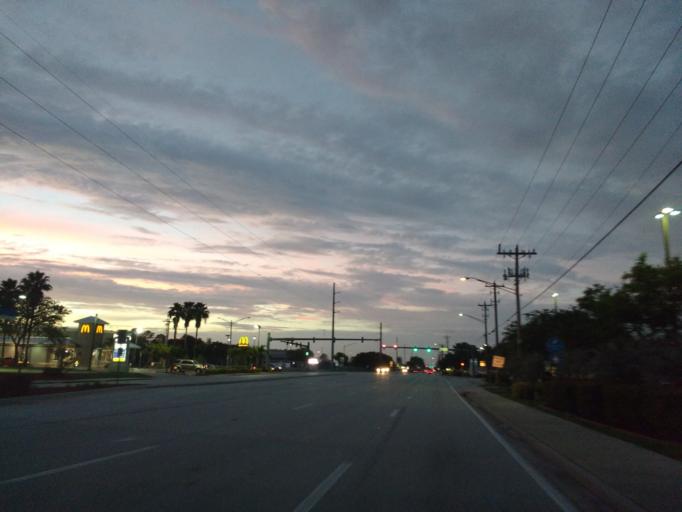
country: US
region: Florida
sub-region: Lee County
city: Cape Coral
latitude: 26.6066
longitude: -81.9742
